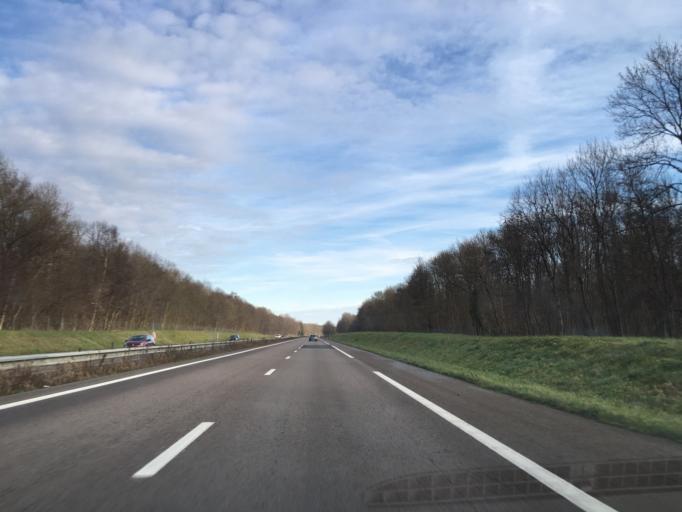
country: FR
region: Picardie
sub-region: Departement de l'Aisne
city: Crezancy
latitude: 49.1162
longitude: 3.5074
